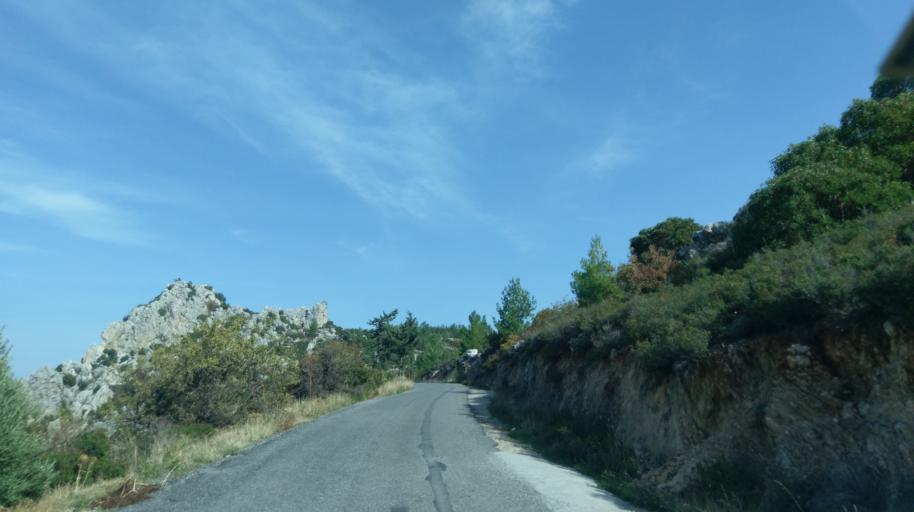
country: CY
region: Keryneia
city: Kyrenia
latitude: 35.3109
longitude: 33.2831
